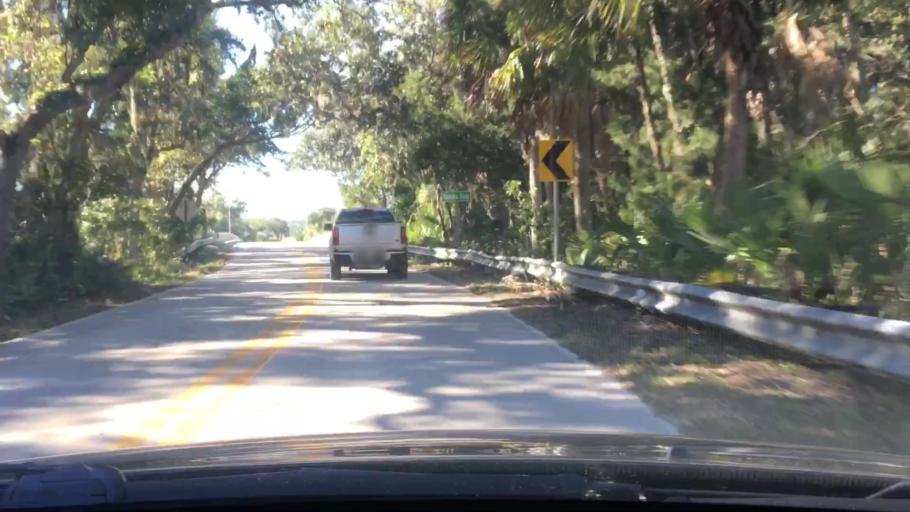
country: US
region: Florida
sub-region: Volusia County
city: Ormond-by-the-Sea
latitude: 29.3422
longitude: -81.0854
